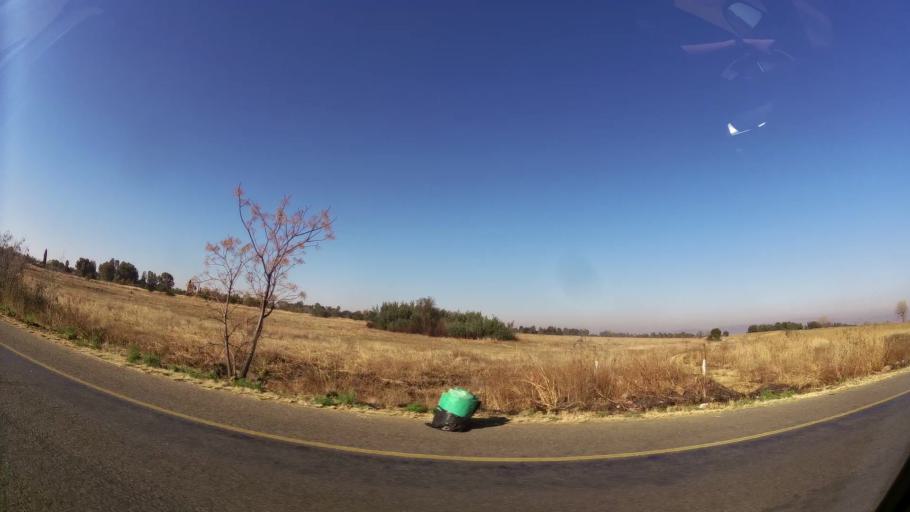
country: ZA
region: Gauteng
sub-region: City of Johannesburg Metropolitan Municipality
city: Johannesburg
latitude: -26.3123
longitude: 28.0864
